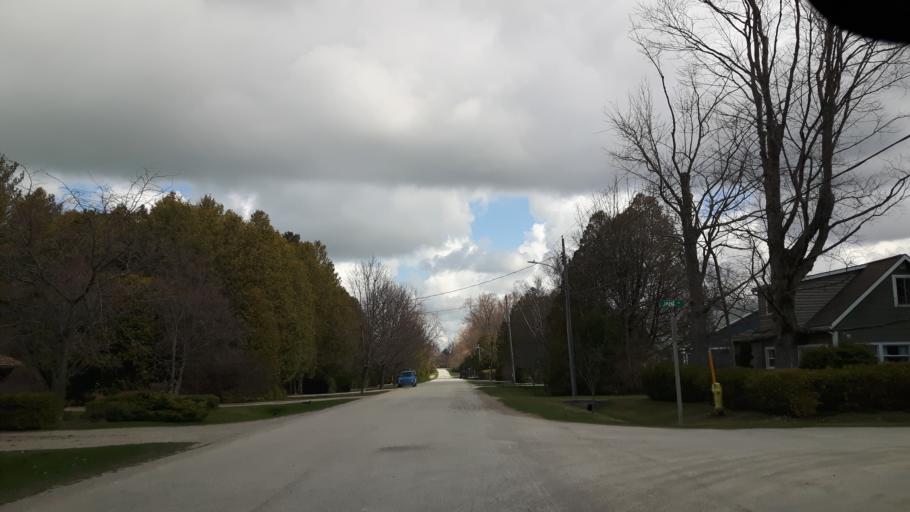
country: CA
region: Ontario
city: Bluewater
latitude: 43.5604
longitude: -81.7047
